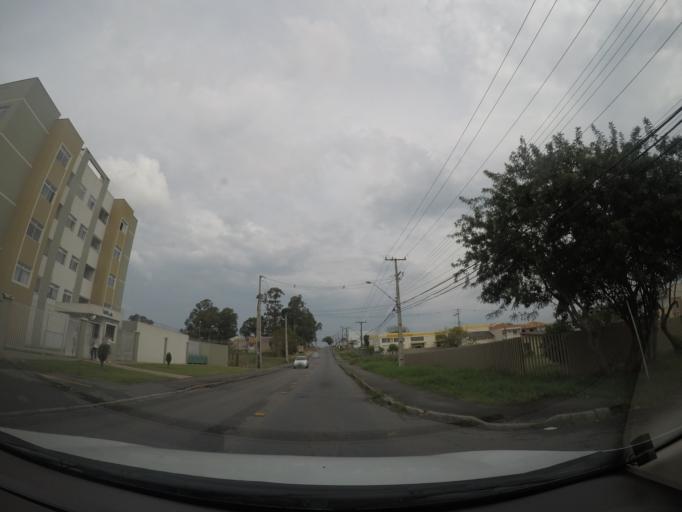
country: BR
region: Parana
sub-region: Sao Jose Dos Pinhais
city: Sao Jose dos Pinhais
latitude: -25.5228
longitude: -49.2611
